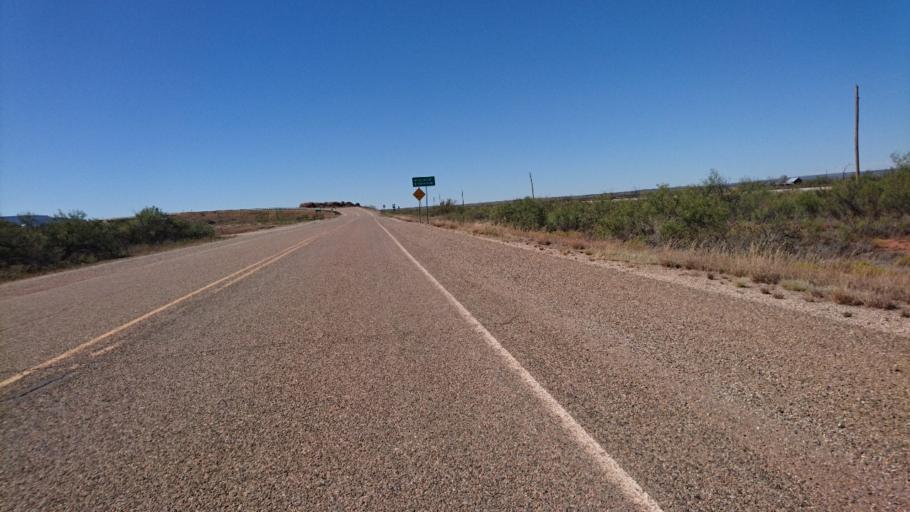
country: US
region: New Mexico
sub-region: Quay County
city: Tucumcari
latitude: 35.0955
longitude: -104.0668
